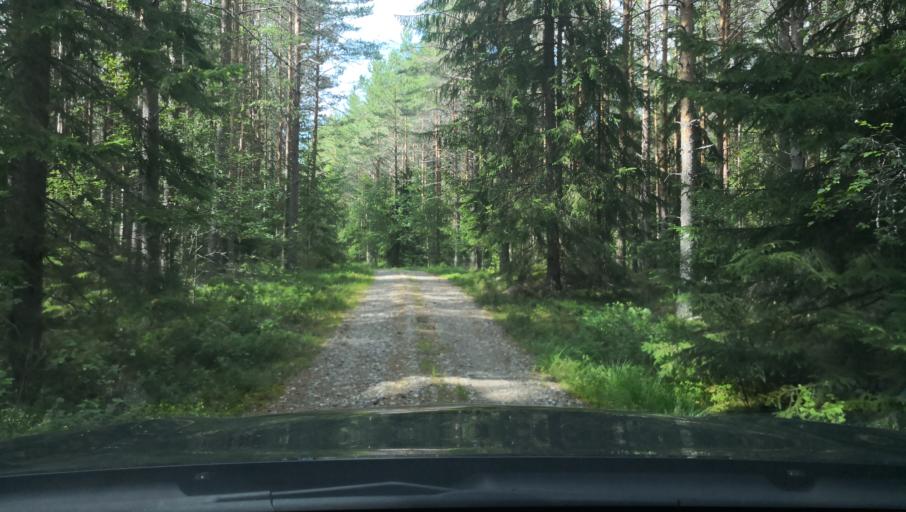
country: SE
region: Vaestmanland
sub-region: Hallstahammars Kommun
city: Hallstahammar
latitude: 59.6493
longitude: 16.0979
